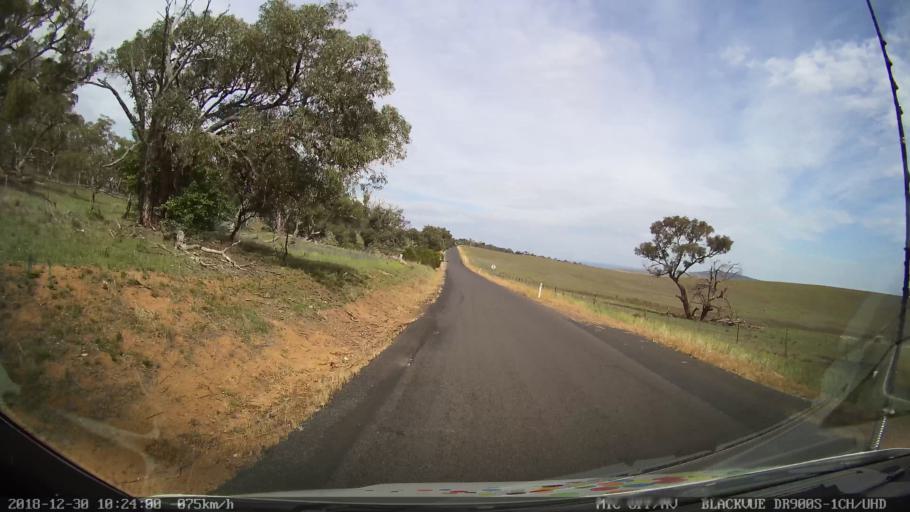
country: AU
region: New South Wales
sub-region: Snowy River
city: Berridale
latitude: -36.5329
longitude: 148.9760
